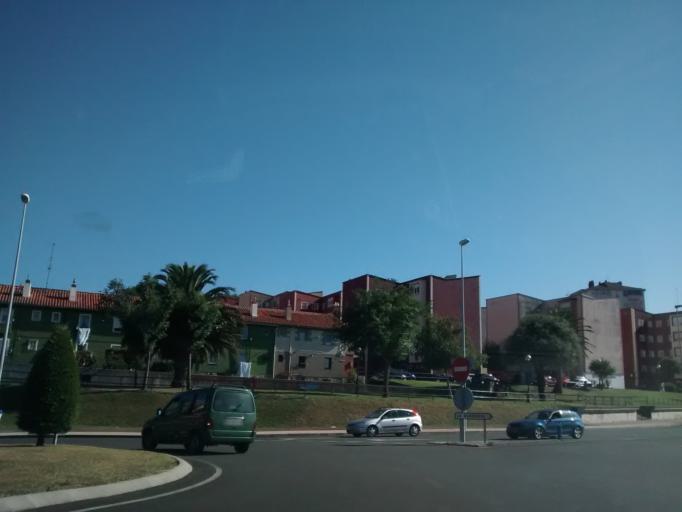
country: ES
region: Cantabria
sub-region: Provincia de Cantabria
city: Santander
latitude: 43.4635
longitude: -3.8326
